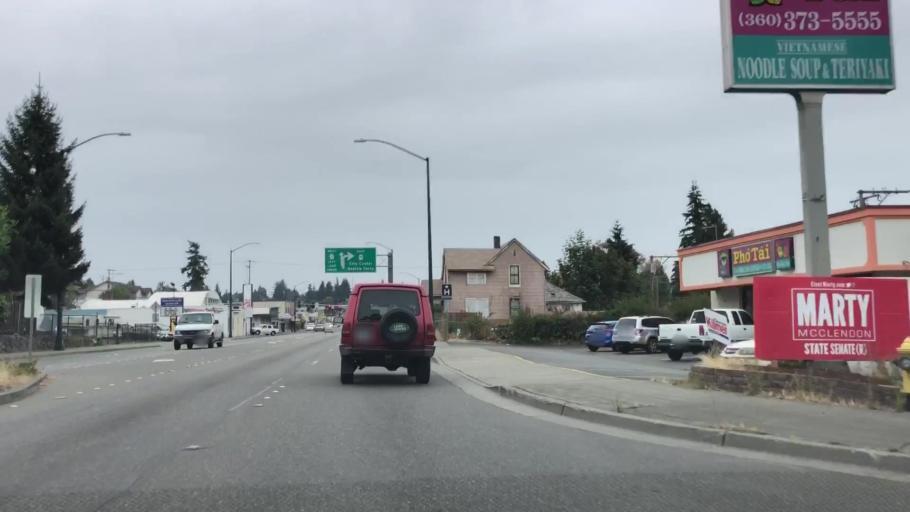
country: US
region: Washington
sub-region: Kitsap County
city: Navy Yard City
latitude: 47.5638
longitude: -122.6532
